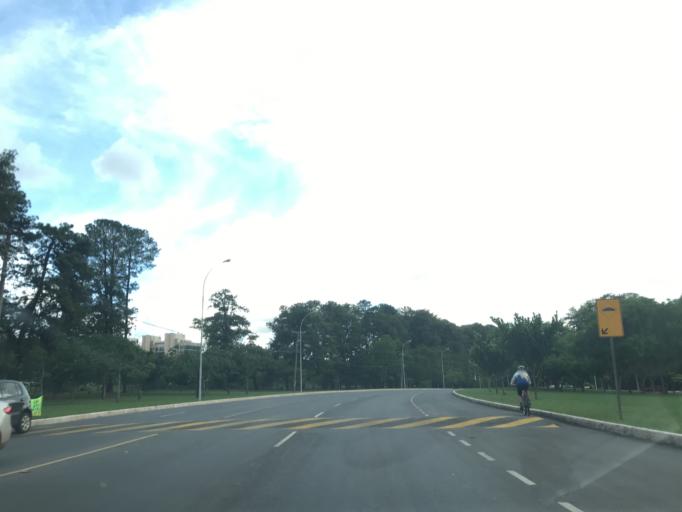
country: BR
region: Federal District
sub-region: Brasilia
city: Brasilia
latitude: -15.8072
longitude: -47.9264
